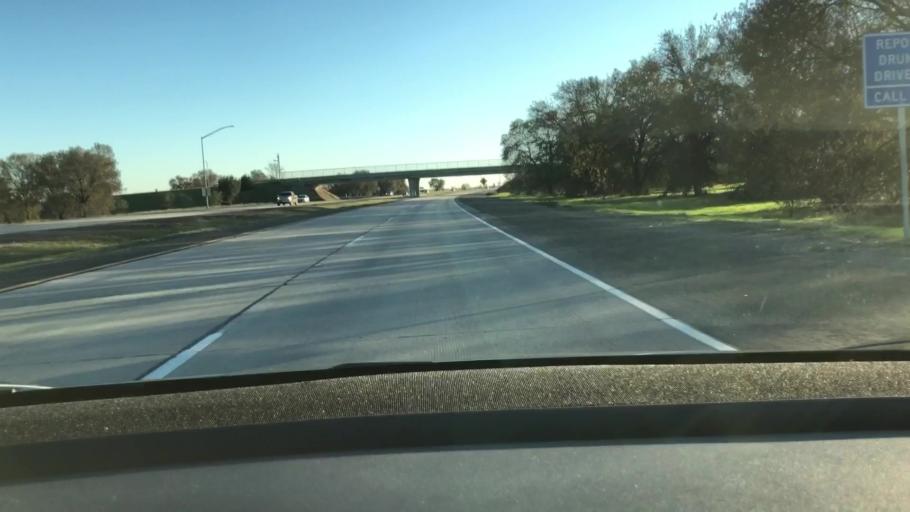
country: US
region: California
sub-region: Yolo County
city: Woodland
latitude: 38.6649
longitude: -121.7514
